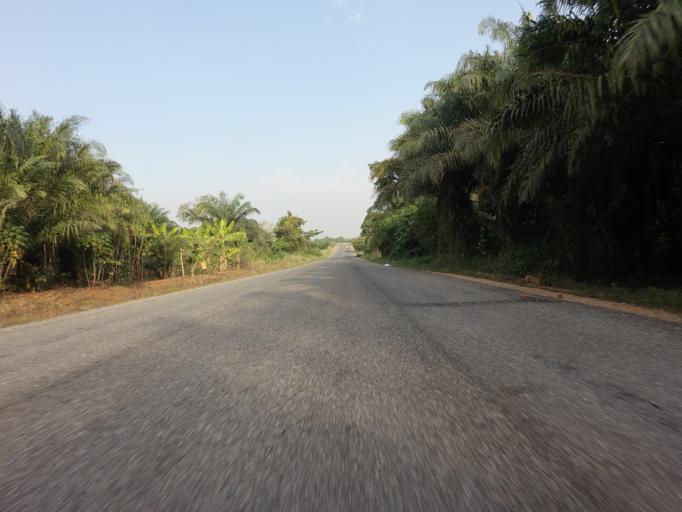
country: GH
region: Volta
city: Ho
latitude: 6.4399
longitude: 0.2009
